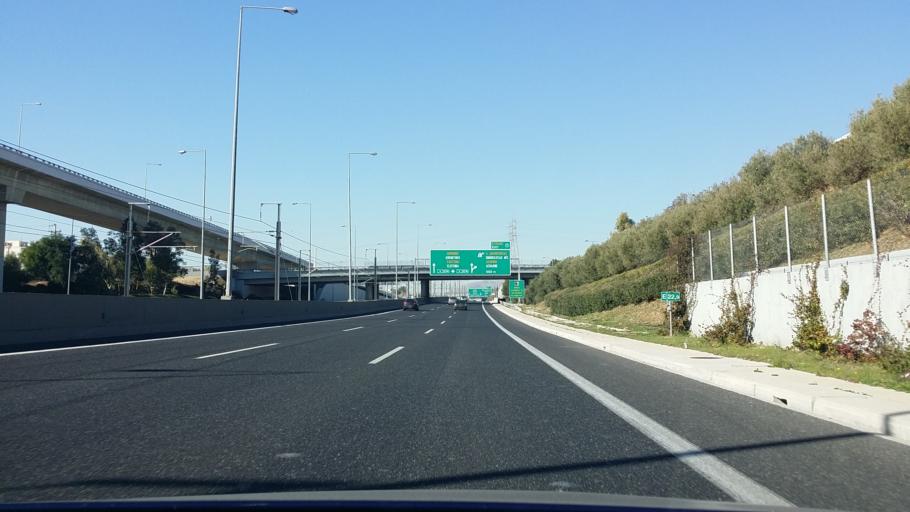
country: GR
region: Attica
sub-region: Nomarchia Athinas
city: Metamorfosi
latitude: 38.0625
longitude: 23.7484
